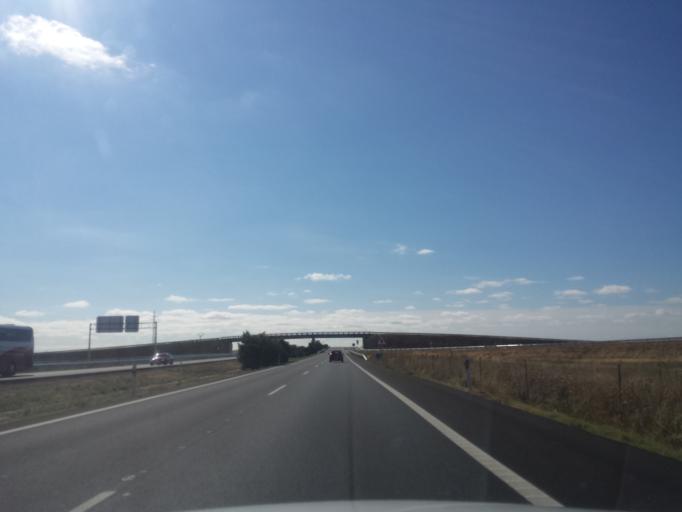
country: ES
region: Castille and Leon
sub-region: Provincia de Zamora
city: Castrogonzalo
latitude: 41.9660
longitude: -5.5918
